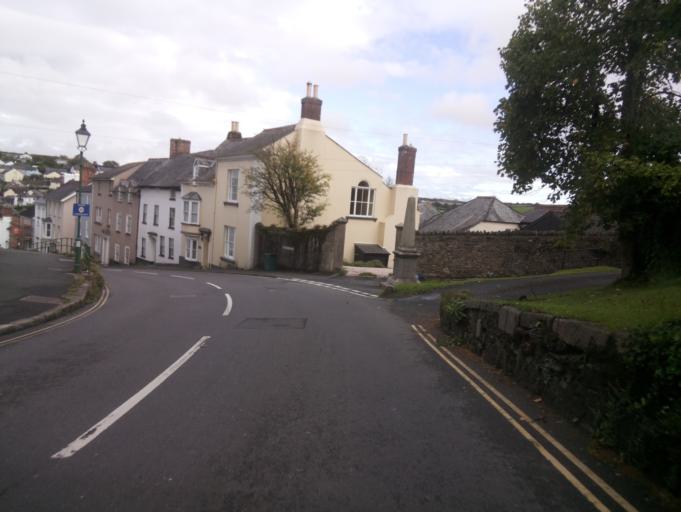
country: GB
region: England
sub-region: Devon
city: Modbury
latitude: 50.3494
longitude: -3.8897
